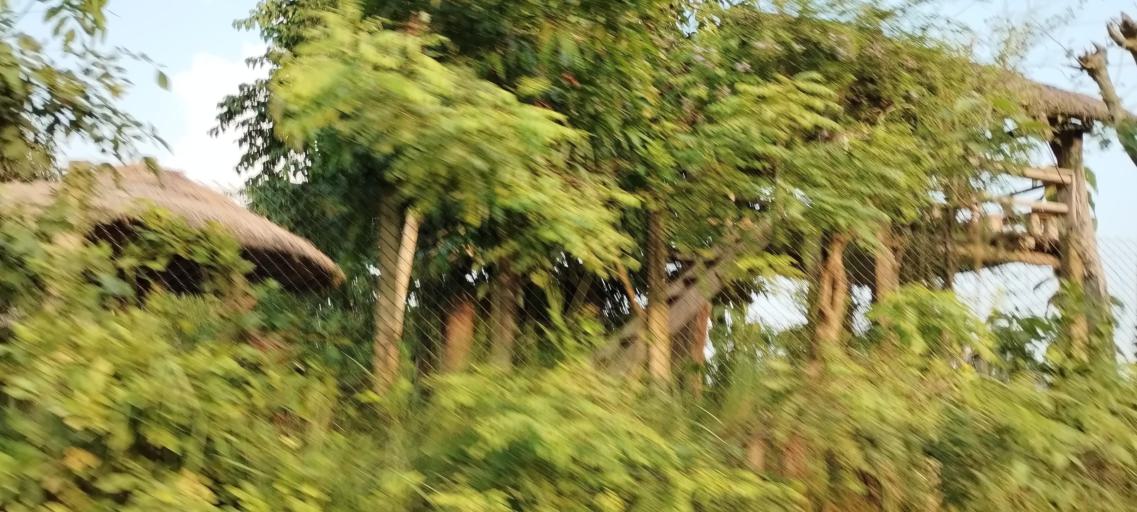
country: NP
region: Far Western
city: Tikapur
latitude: 28.4498
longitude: 81.2393
